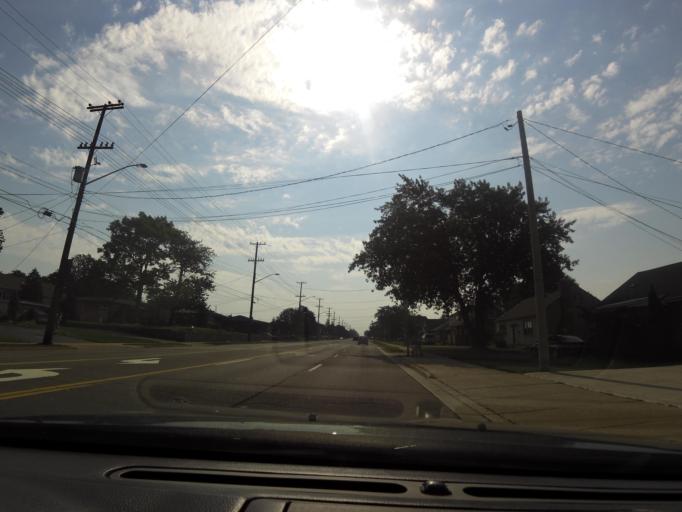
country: CA
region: Ontario
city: Hamilton
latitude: 43.2279
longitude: -79.8787
